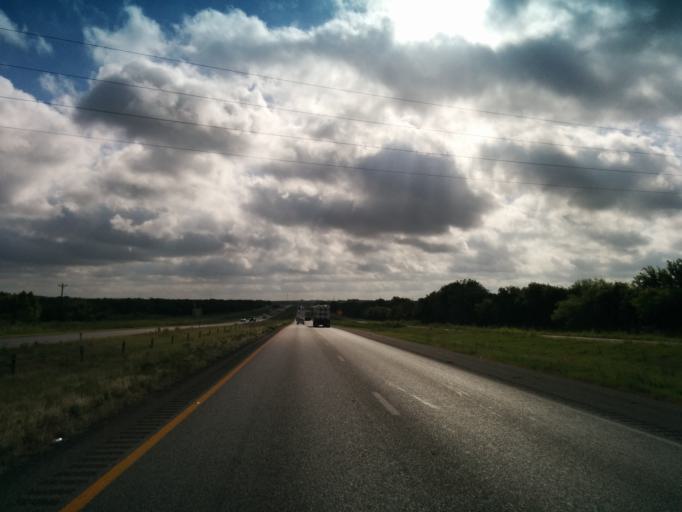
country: US
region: Texas
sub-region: Guadalupe County
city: Marion
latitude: 29.5240
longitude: -98.1255
